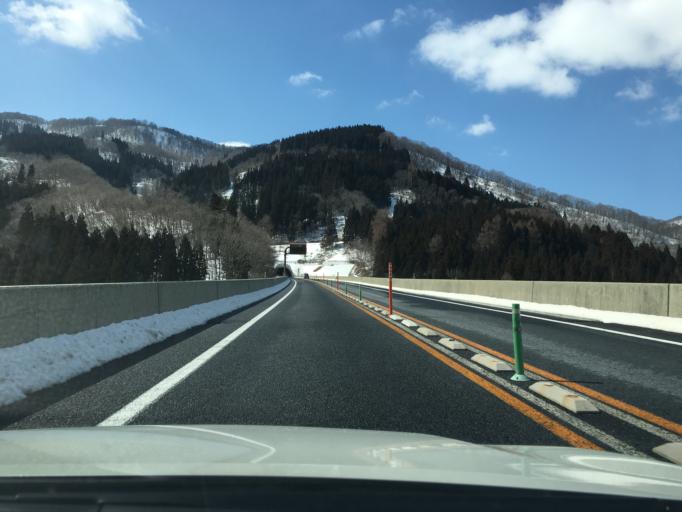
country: JP
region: Yamagata
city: Sagae
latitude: 38.4449
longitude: 140.0517
